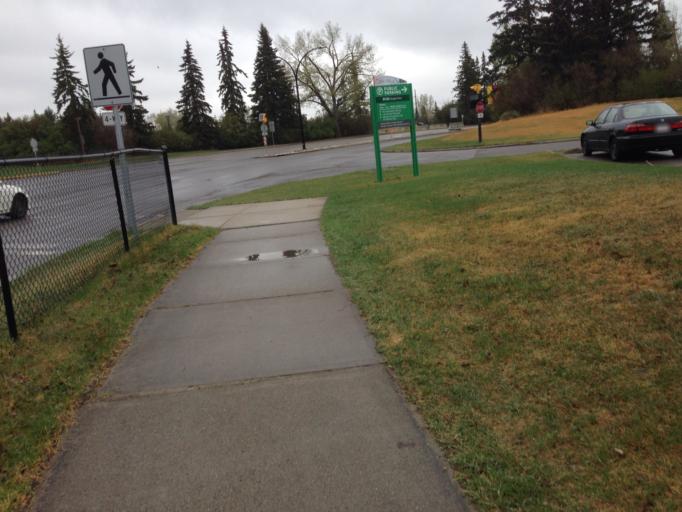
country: CA
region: Alberta
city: Calgary
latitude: 51.0788
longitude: -114.1368
